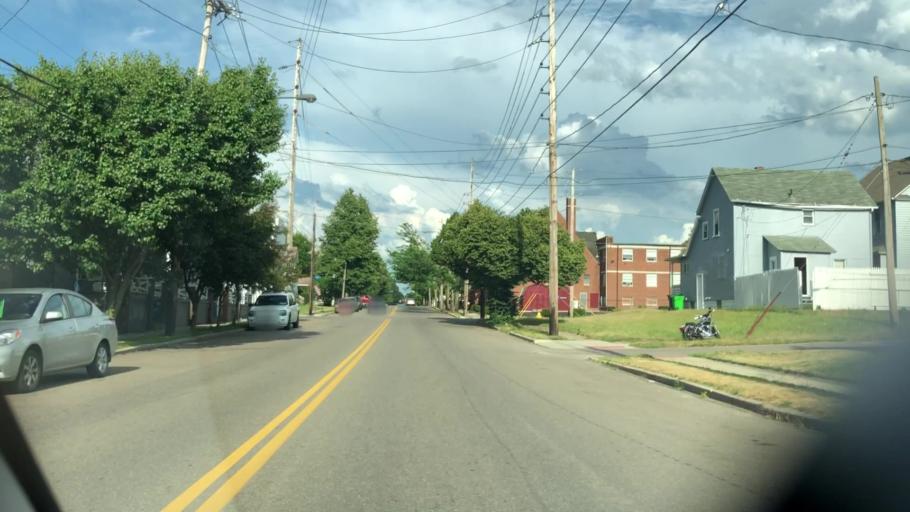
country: US
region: Ohio
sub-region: Summit County
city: Barberton
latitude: 41.0178
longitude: -81.6143
